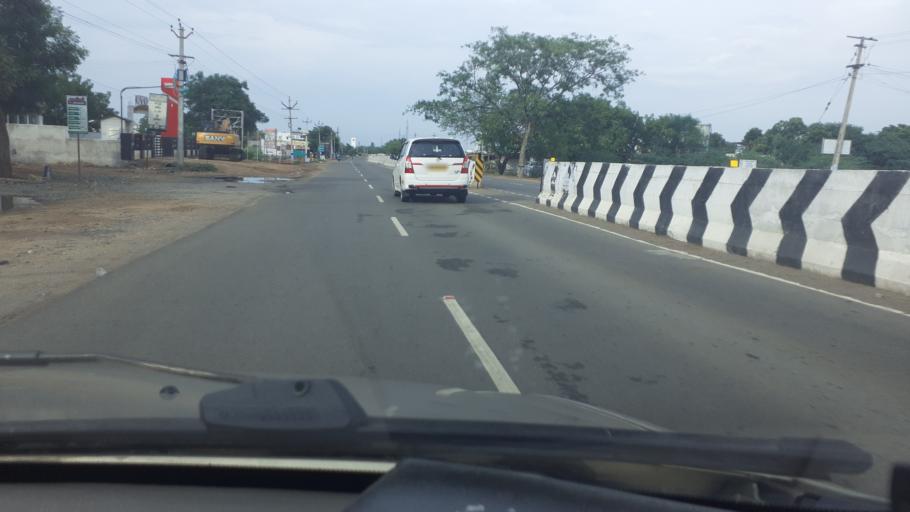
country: IN
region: Tamil Nadu
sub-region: Tirunelveli Kattabo
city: Tirunelveli
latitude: 8.6641
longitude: 77.7159
